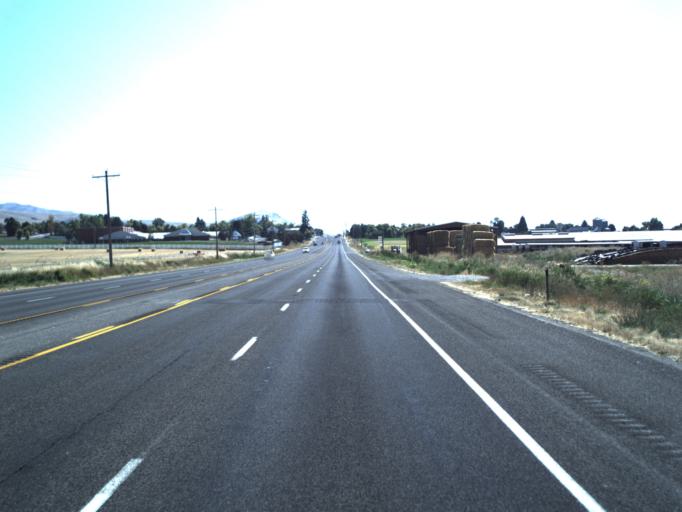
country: US
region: Utah
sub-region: Cache County
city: Richmond
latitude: 41.9316
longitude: -111.8142
